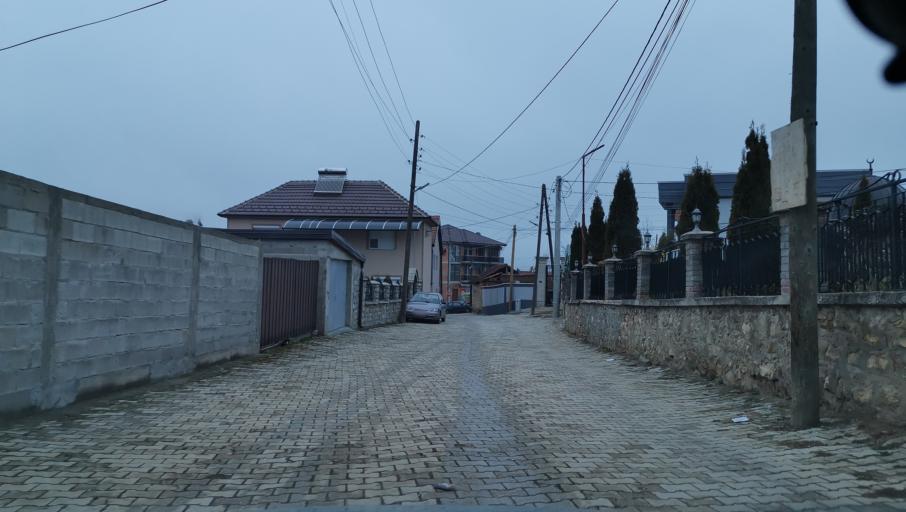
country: MK
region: Debar
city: Debar
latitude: 41.5280
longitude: 20.5237
